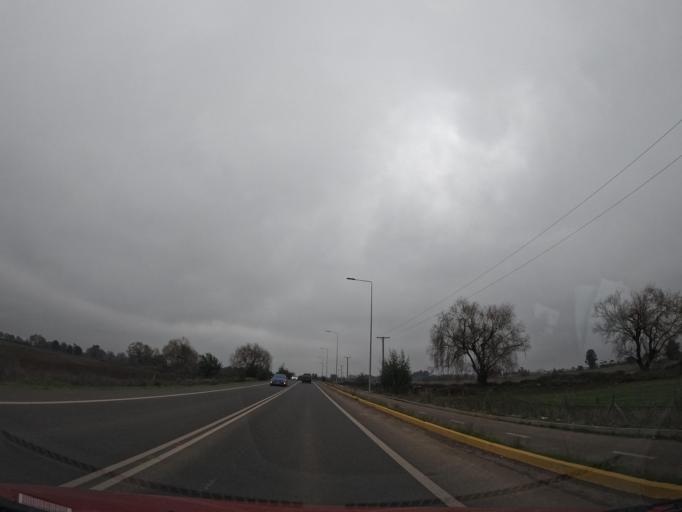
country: CL
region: Maule
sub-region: Provincia de Talca
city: San Clemente
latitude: -35.5362
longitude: -71.4733
